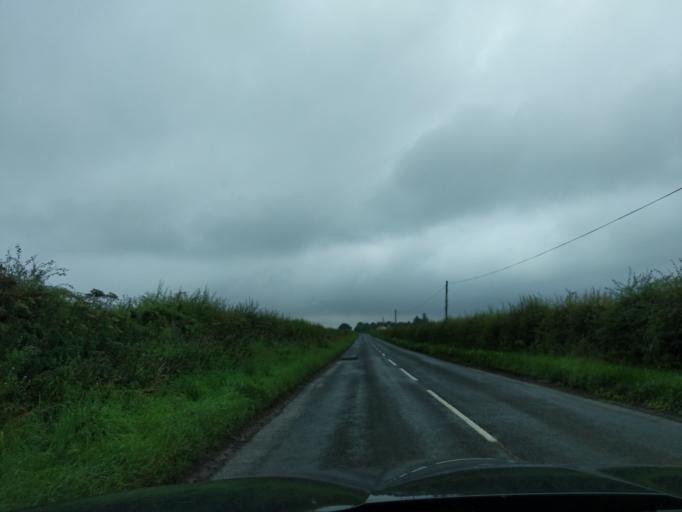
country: GB
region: England
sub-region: Northumberland
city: Ford
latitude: 55.6452
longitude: -2.0414
